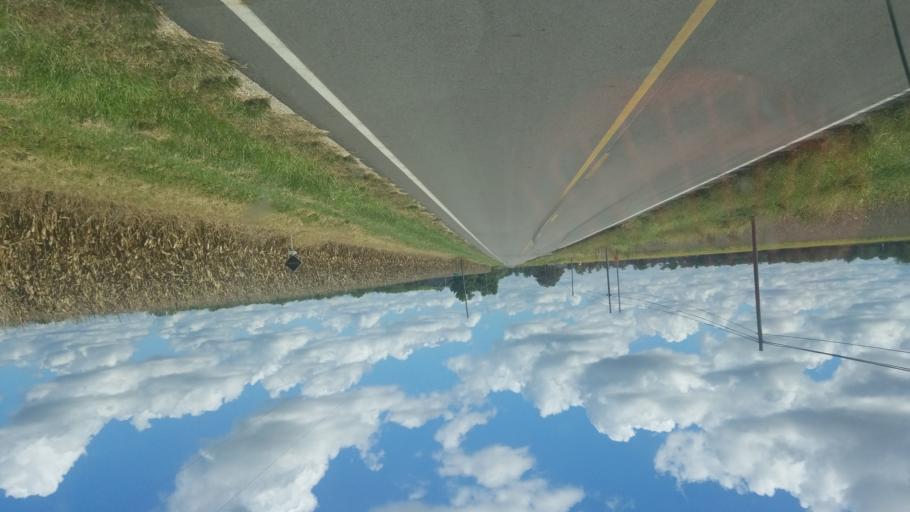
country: US
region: Ohio
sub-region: Union County
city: Marysville
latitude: 40.1867
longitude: -83.4584
